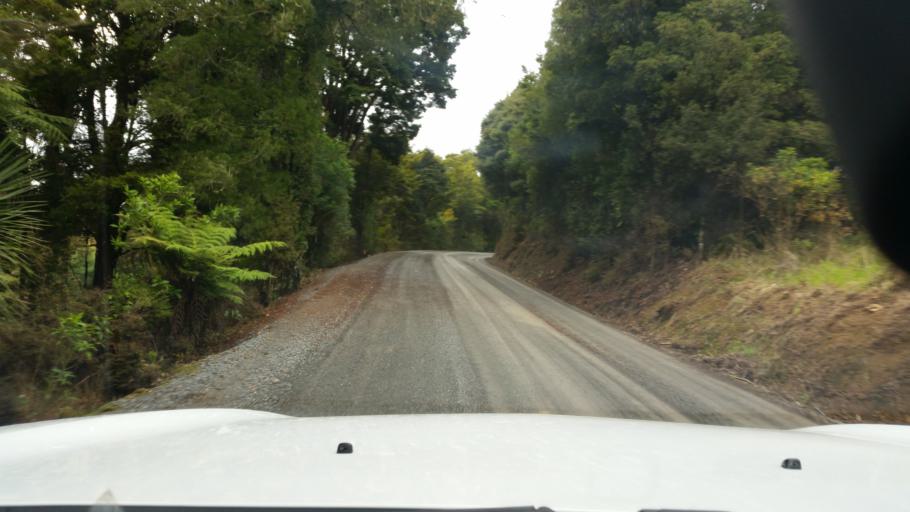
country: NZ
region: Northland
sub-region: Whangarei
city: Whangarei
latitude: -35.7343
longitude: 174.4319
